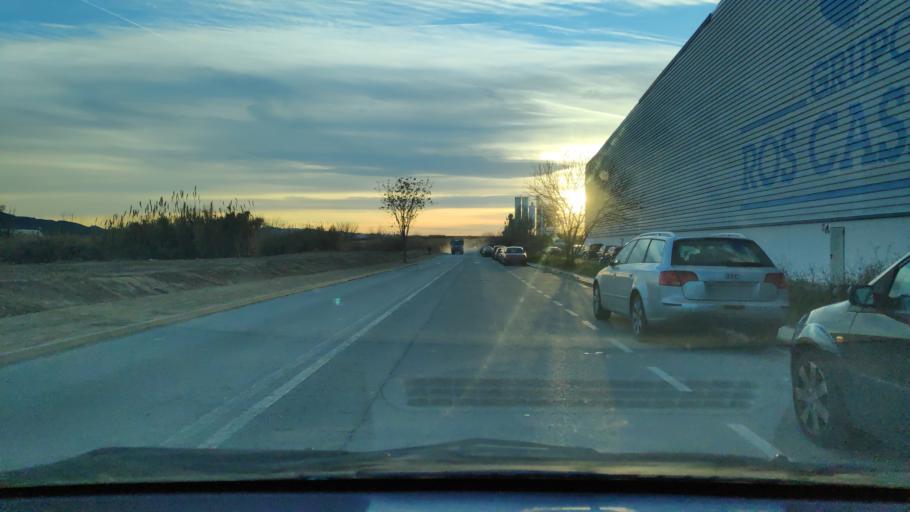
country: ES
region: Catalonia
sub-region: Provincia de Barcelona
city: Montmelo
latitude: 41.5449
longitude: 2.2359
